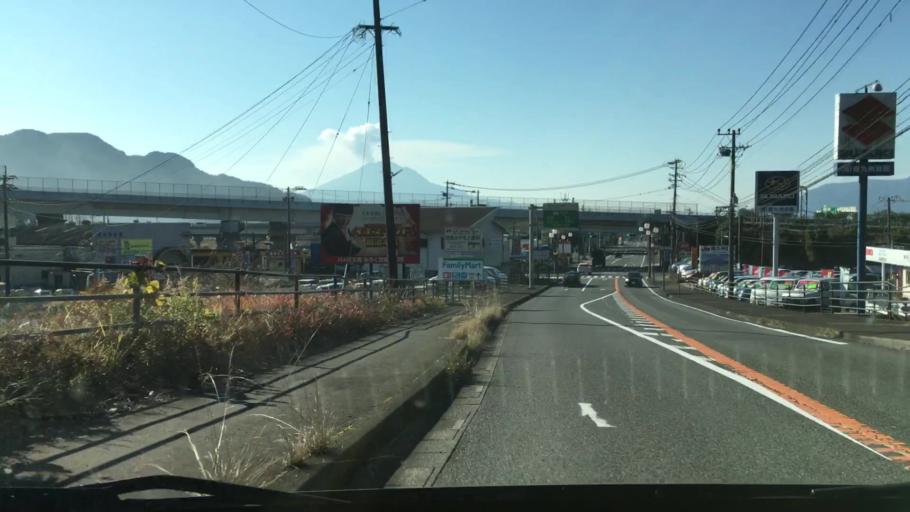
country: JP
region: Kagoshima
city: Kajiki
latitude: 31.7485
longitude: 130.6712
